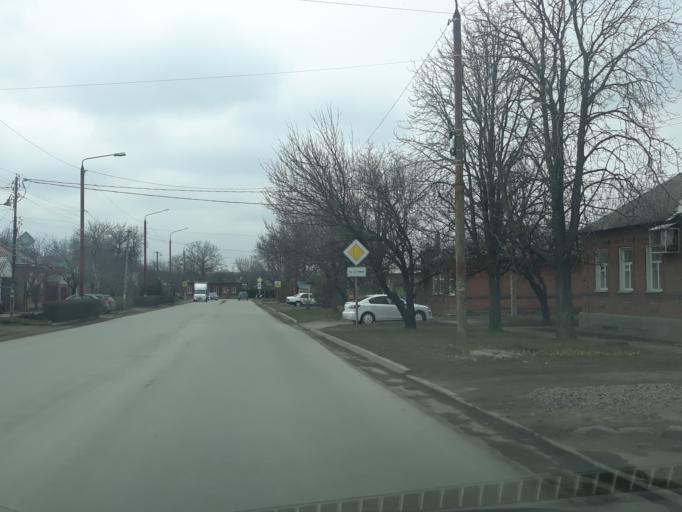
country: RU
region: Rostov
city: Taganrog
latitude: 47.2675
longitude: 38.8932
